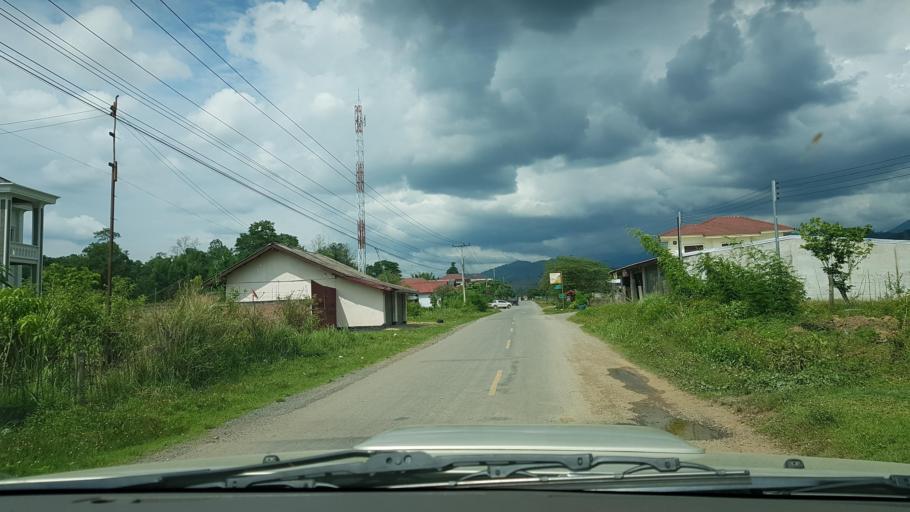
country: LA
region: Loungnamtha
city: Muang Nale
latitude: 20.2855
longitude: 101.6205
